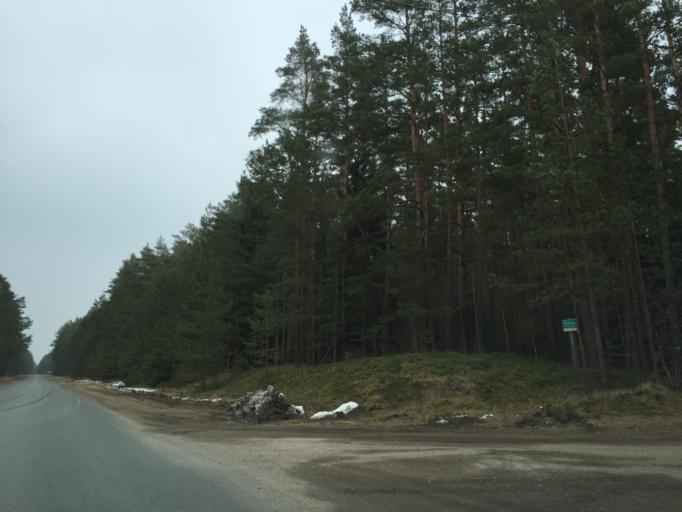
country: LV
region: Salacgrivas
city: Ainazi
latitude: 57.9870
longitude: 24.4225
